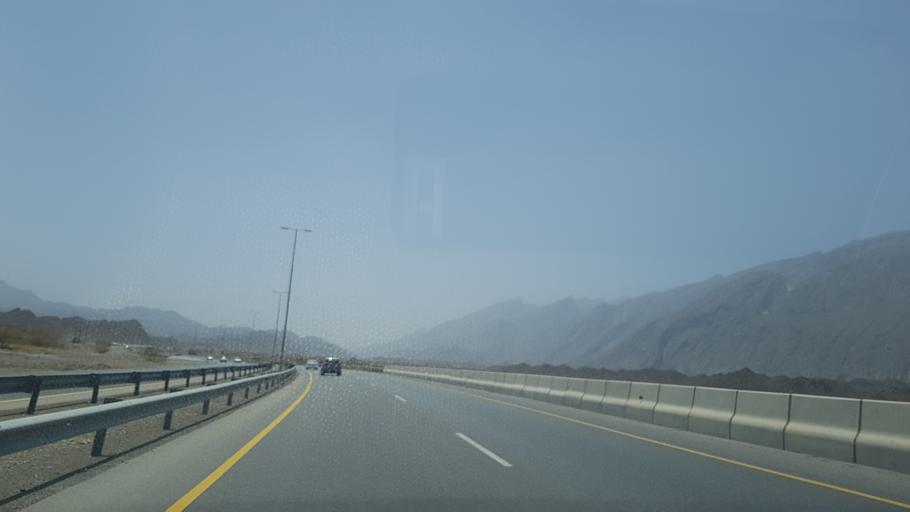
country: OM
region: Muhafazat ad Dakhiliyah
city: Sufalat Sama'il
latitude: 23.2310
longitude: 57.9042
